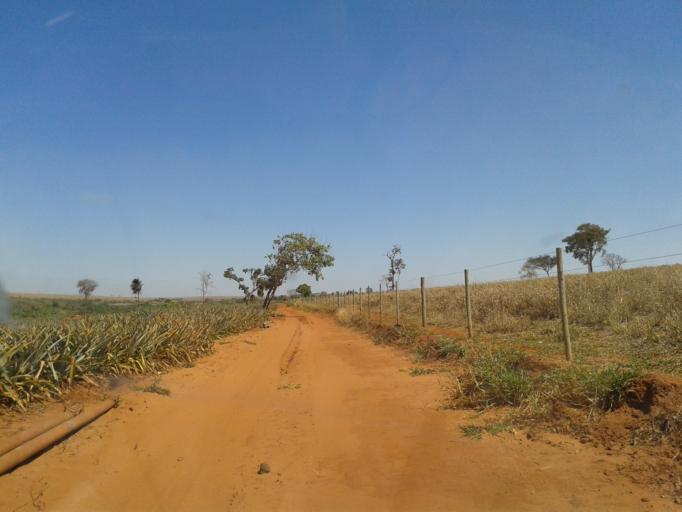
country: BR
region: Minas Gerais
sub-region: Monte Alegre De Minas
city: Monte Alegre de Minas
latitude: -18.8285
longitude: -49.1281
